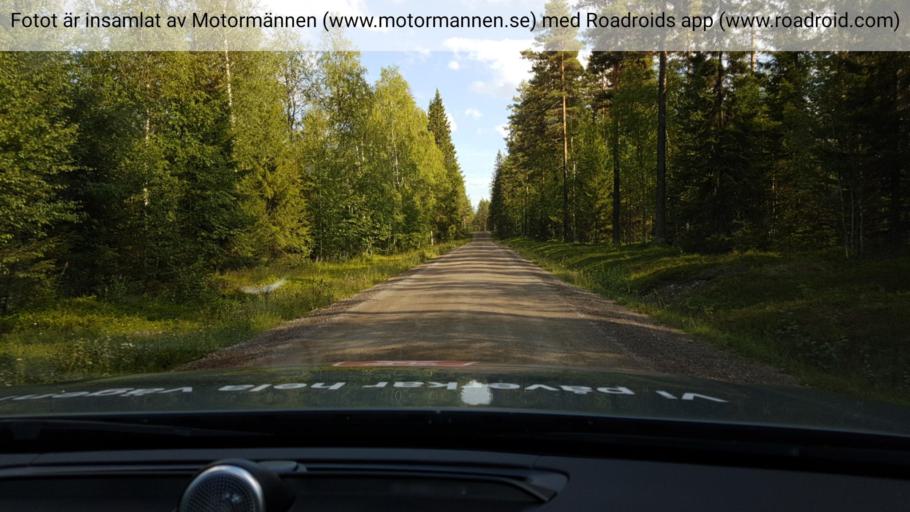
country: SE
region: Vaesterbotten
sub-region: Dorotea Kommun
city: Dorotea
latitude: 63.9766
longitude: 16.0471
